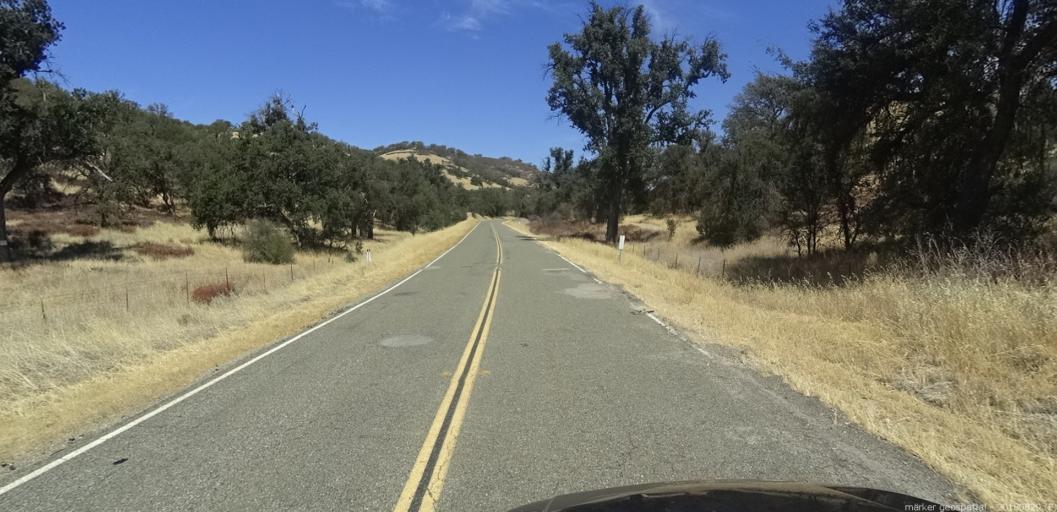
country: US
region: California
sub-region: San Luis Obispo County
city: Lake Nacimiento
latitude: 35.9083
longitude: -121.0875
